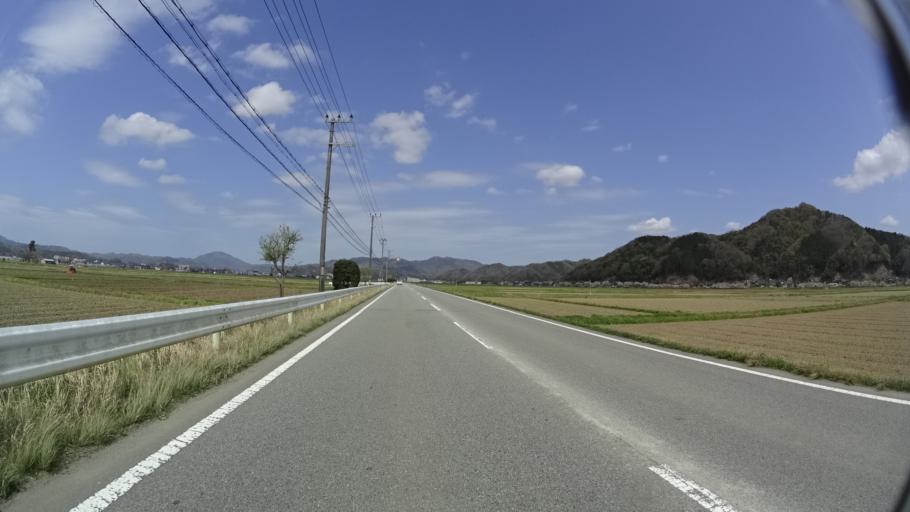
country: JP
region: Hyogo
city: Toyooka
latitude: 35.5154
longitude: 134.8399
